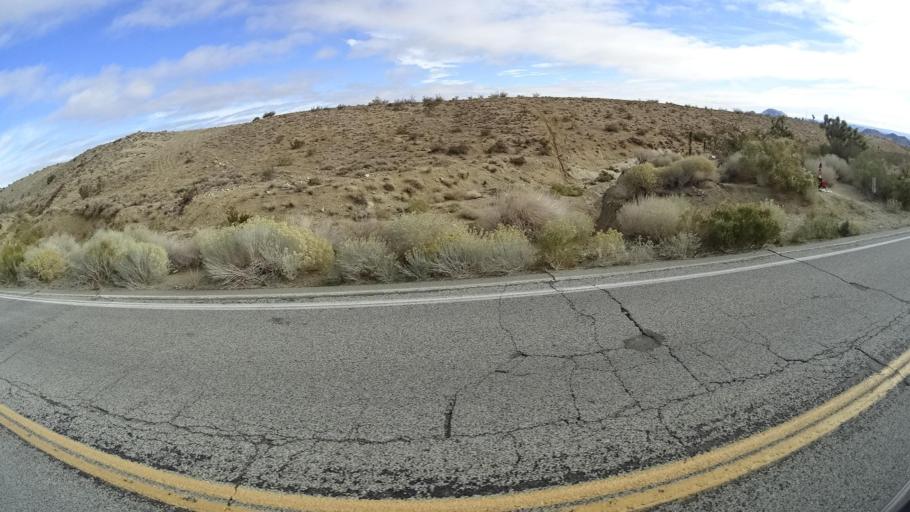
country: US
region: California
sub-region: Kern County
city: Tehachapi
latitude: 35.0038
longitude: -118.3389
